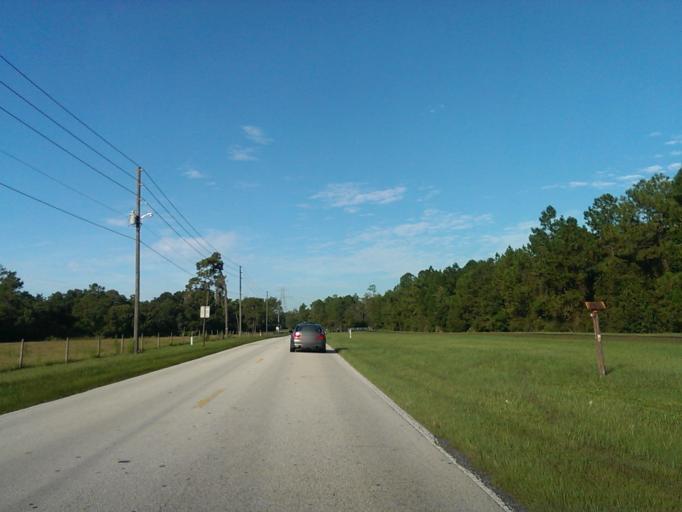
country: US
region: Florida
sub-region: Orange County
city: Lake Butler
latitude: 28.4652
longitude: -81.5898
